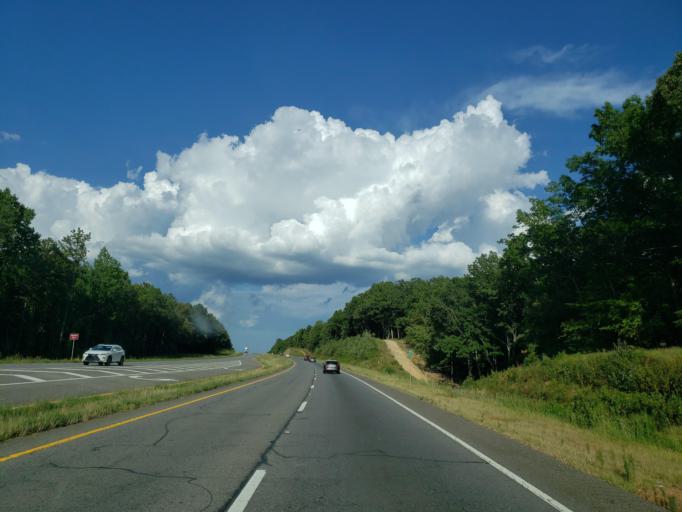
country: US
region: Georgia
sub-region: Bartow County
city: Euharlee
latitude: 34.2110
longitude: -84.9619
